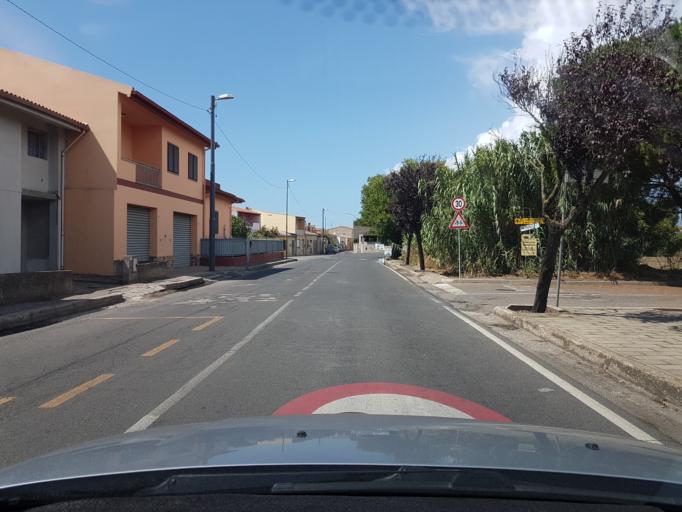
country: IT
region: Sardinia
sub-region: Provincia di Oristano
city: Donigala Fenugheddu
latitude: 39.9332
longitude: 8.5733
